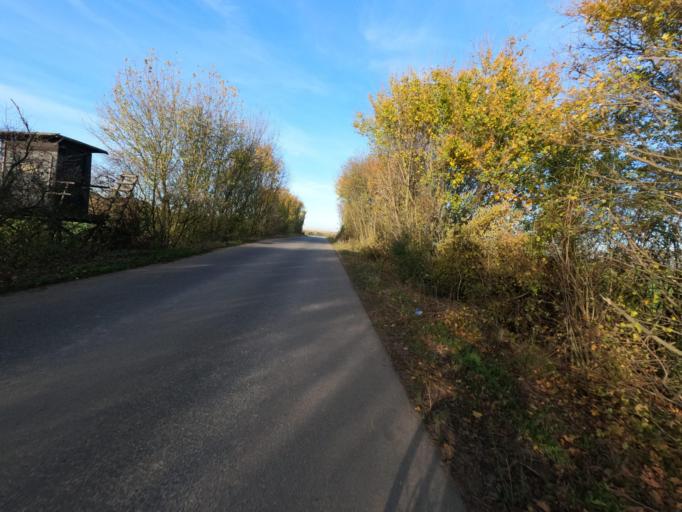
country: DE
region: North Rhine-Westphalia
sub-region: Regierungsbezirk Koln
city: Titz
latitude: 51.0419
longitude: 6.4616
